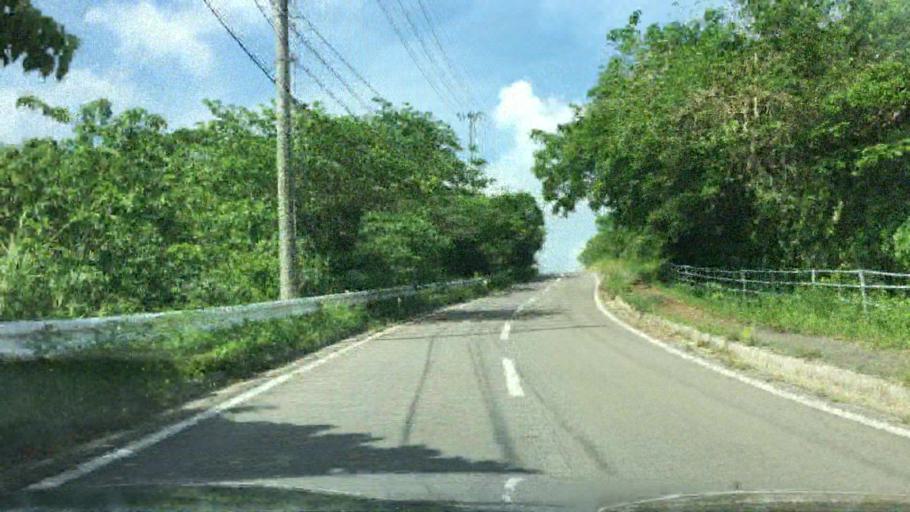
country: JP
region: Okinawa
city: Ishigaki
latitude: 24.4890
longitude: 124.2317
